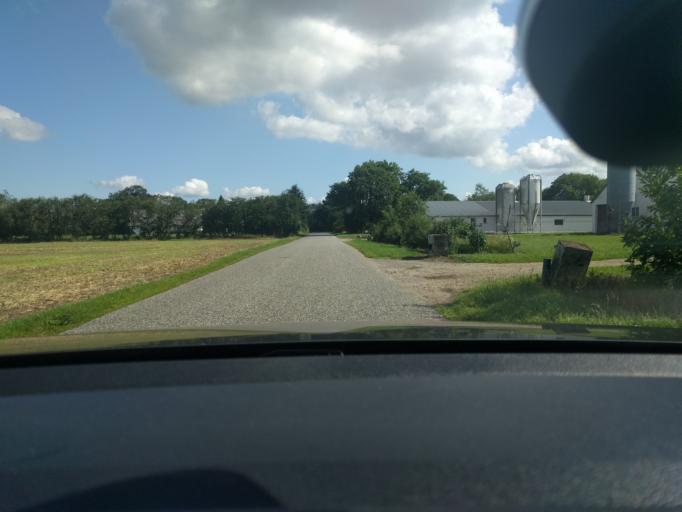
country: DK
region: Central Jutland
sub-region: Viborg Kommune
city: Stoholm
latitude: 56.4707
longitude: 9.2617
